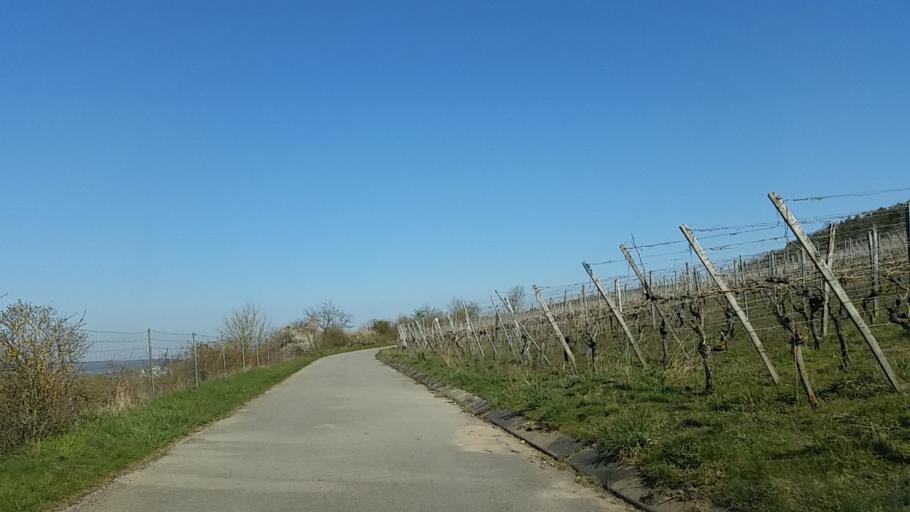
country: DE
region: Bavaria
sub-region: Regierungsbezirk Unterfranken
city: Zellingen
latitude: 49.9162
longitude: 9.8222
